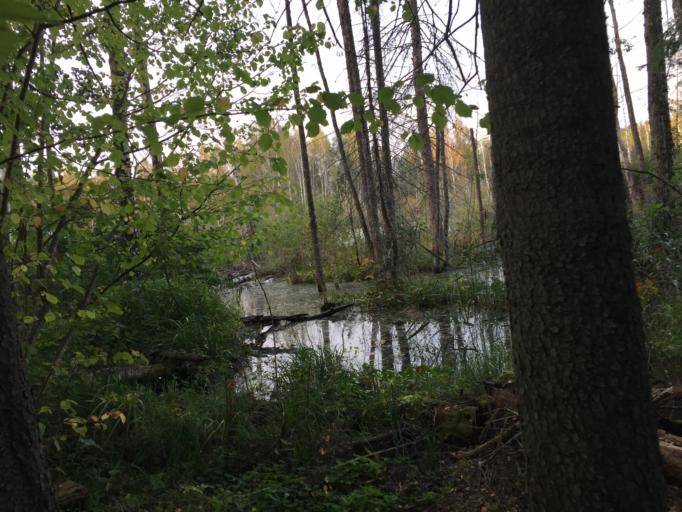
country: LV
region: Baldone
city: Baldone
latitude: 56.7574
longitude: 24.4034
